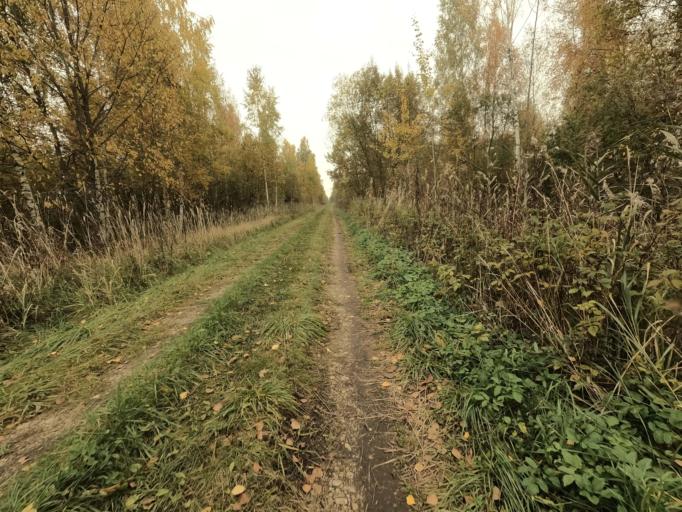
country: RU
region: Novgorod
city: Pankovka
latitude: 58.8811
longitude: 30.9435
